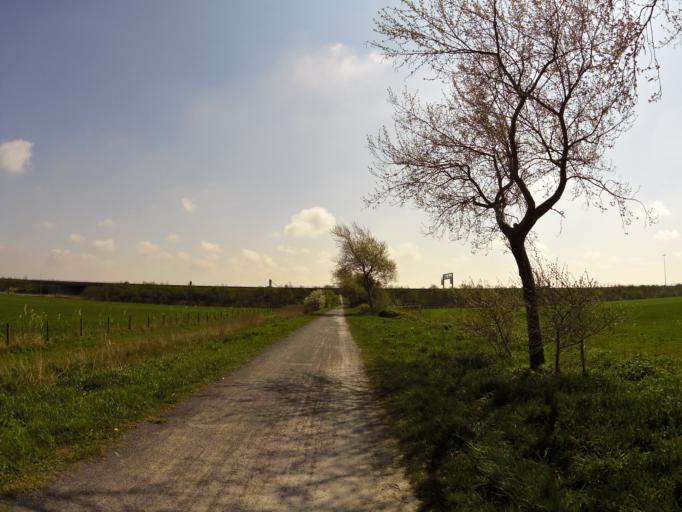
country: BE
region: Flanders
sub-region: Provincie West-Vlaanderen
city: Nieuwpoort
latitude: 51.1178
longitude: 2.7615
